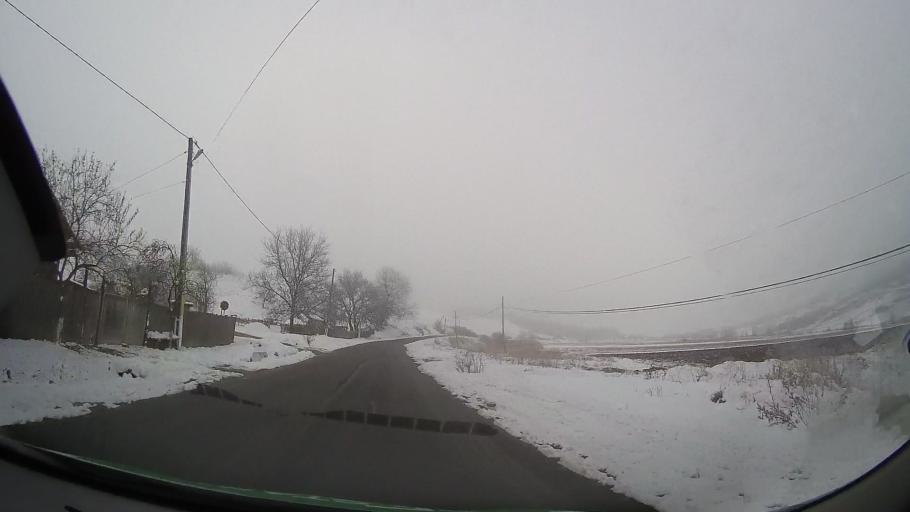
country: RO
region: Bacau
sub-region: Comuna Oncesti
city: Oncesti
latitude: 46.4835
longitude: 27.2563
